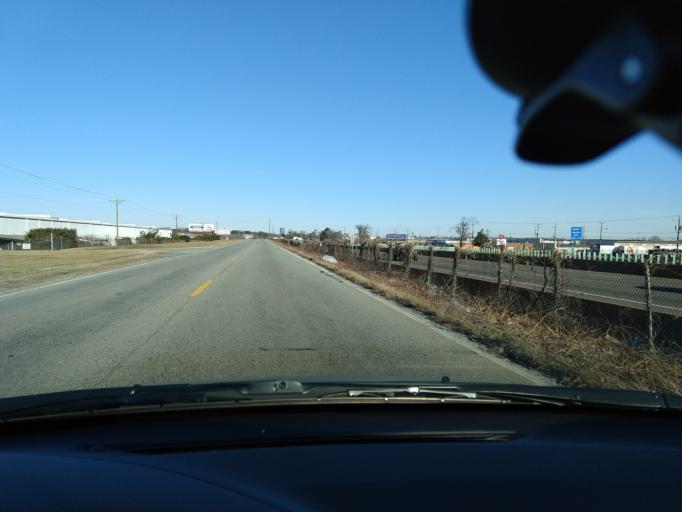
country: US
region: Virginia
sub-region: Chesterfield County
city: Bensley
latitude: 37.4846
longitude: -77.4320
